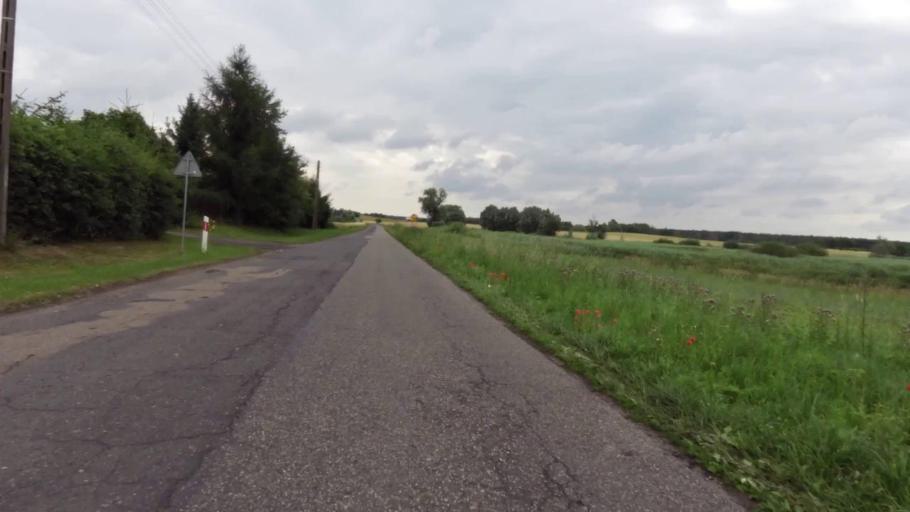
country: PL
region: West Pomeranian Voivodeship
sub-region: Powiat mysliborski
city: Mysliborz
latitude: 52.9526
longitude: 14.8785
